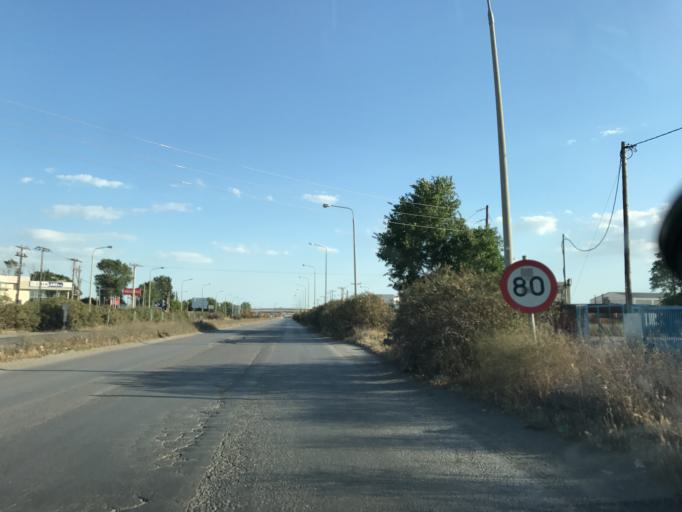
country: GR
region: Central Macedonia
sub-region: Nomos Thessalonikis
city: Menemeni
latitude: 40.6632
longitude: 22.8816
